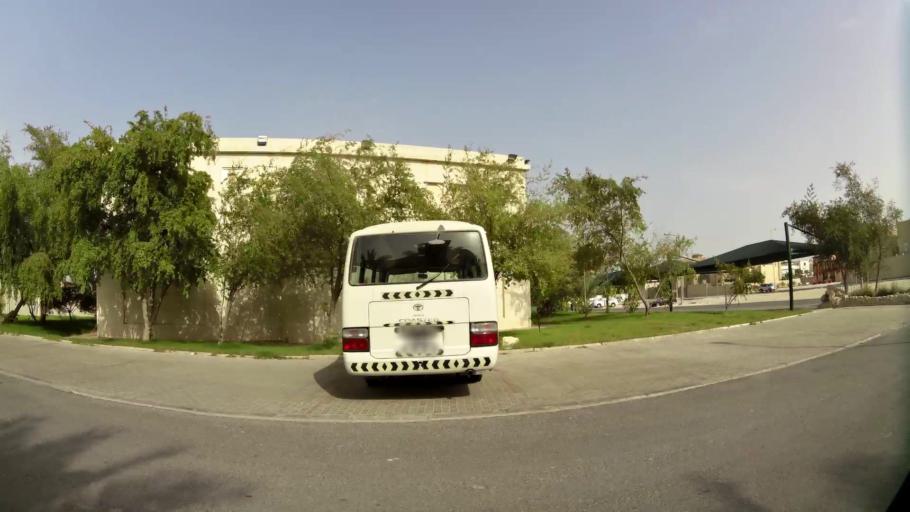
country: QA
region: Baladiyat ad Dawhah
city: Doha
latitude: 25.3227
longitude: 51.5022
